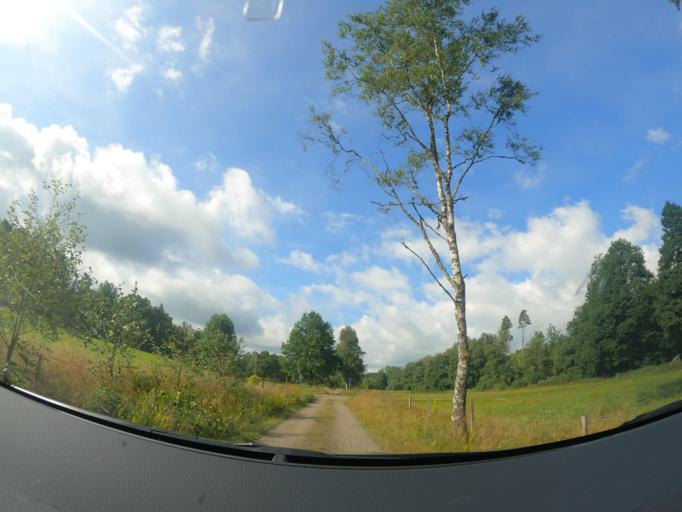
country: SE
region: Vaestra Goetaland
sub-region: Marks Kommun
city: Horred
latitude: 57.1685
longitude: 12.7590
